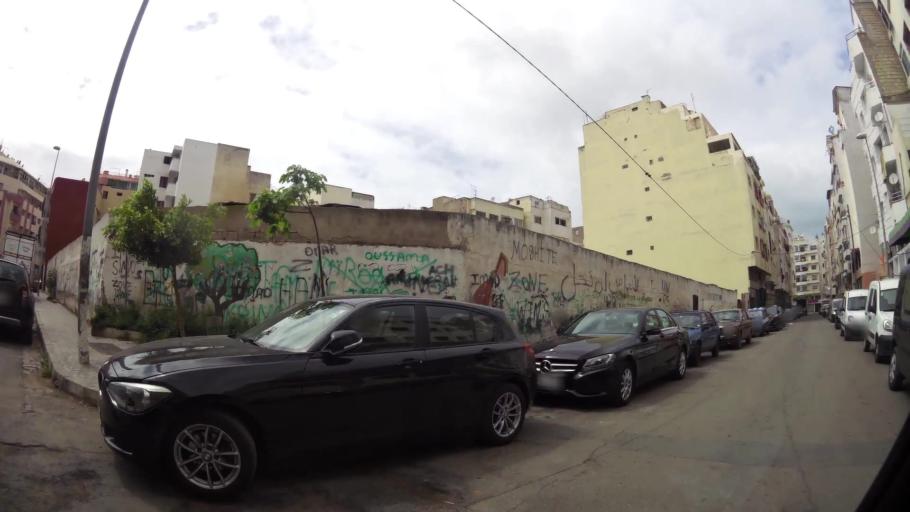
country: MA
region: Grand Casablanca
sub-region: Casablanca
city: Casablanca
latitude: 33.6000
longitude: -7.6443
